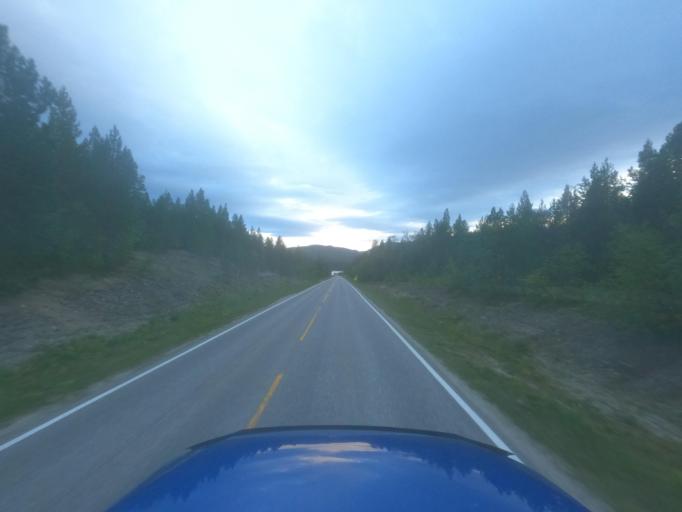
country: NO
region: Finnmark Fylke
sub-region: Porsanger
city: Lakselv
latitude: 69.8993
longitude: 24.9983
